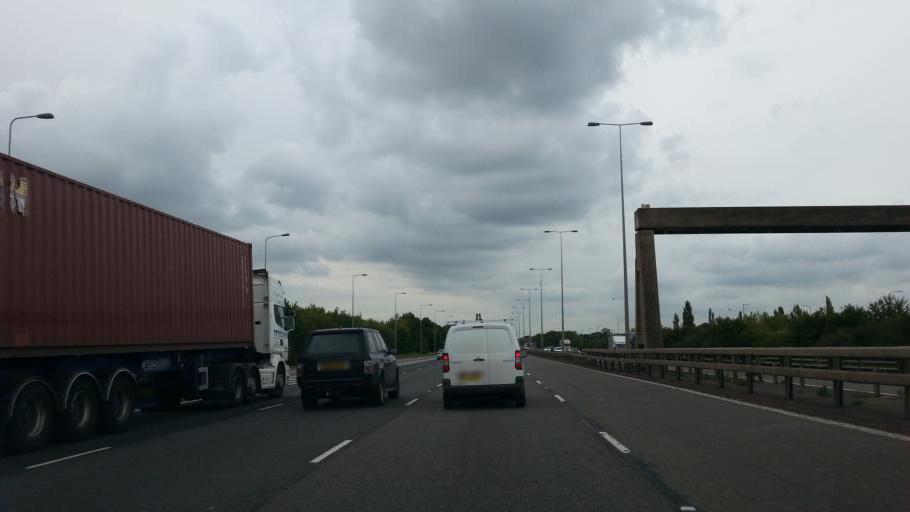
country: GB
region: England
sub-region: Cambridgeshire
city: Sawtry
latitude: 52.4322
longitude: -0.2714
